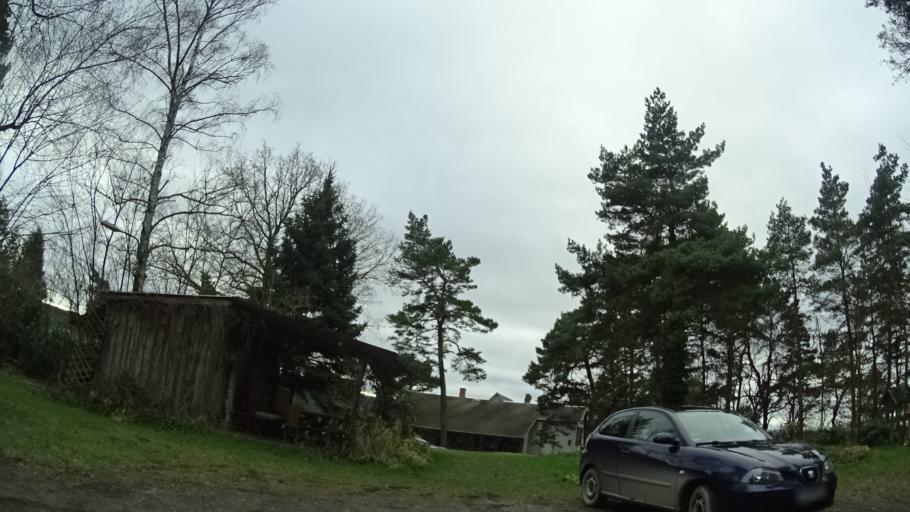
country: DE
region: Thuringia
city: Orlamunde
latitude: 50.7465
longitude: 11.4684
